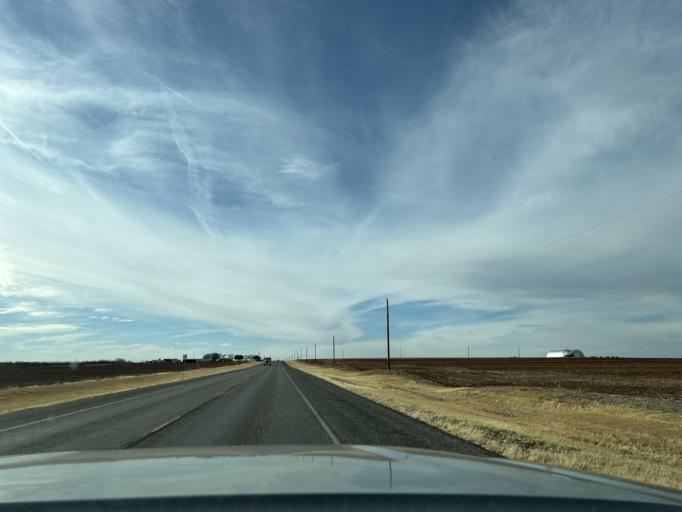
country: US
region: Texas
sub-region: Jones County
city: Anson
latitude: 32.7519
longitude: -99.9402
